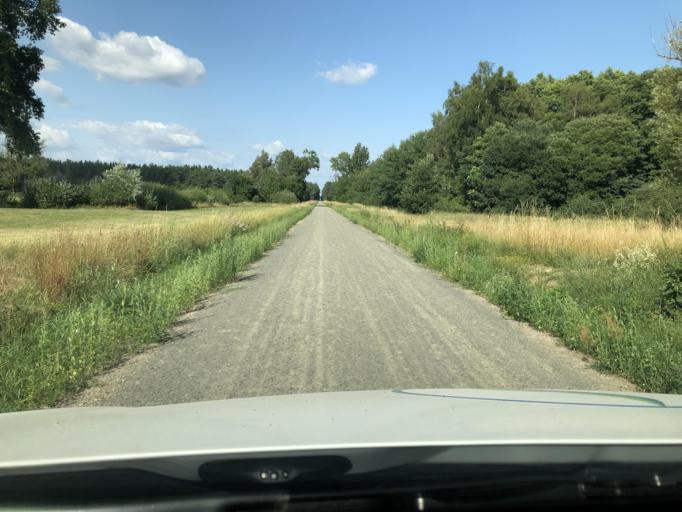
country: SE
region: Skane
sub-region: Kristianstads Kommun
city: Norra Asum
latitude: 55.9117
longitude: 14.1137
